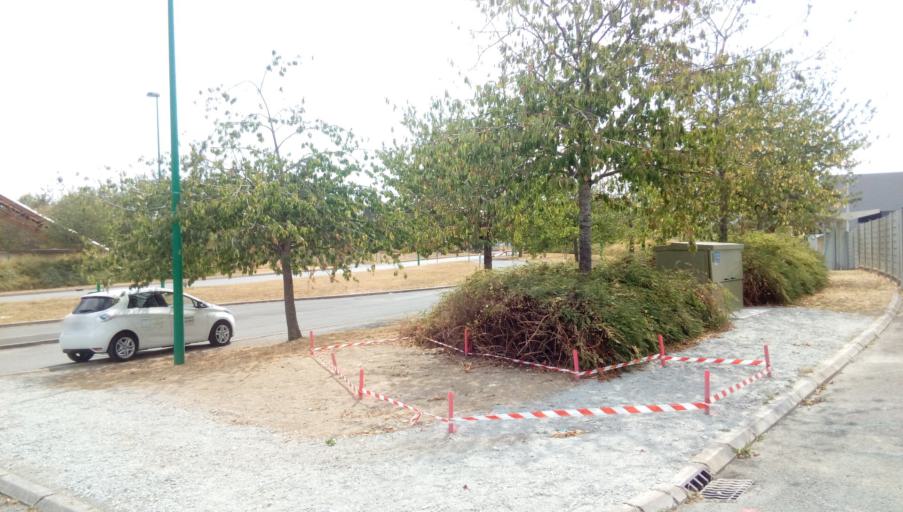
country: FR
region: Limousin
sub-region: Departement de la Creuse
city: Gueret
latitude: 46.1983
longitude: 1.8866
